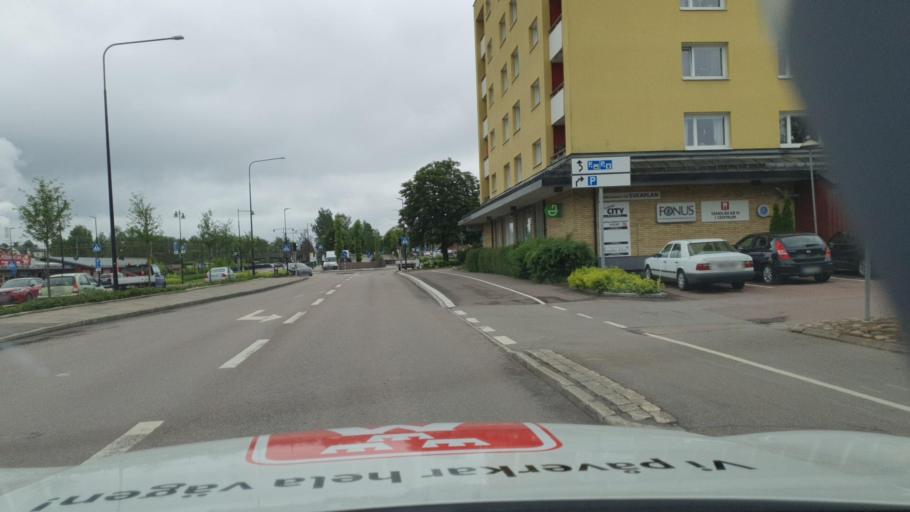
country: SE
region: Vaermland
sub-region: Grums Kommun
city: Grums
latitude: 59.3536
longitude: 13.1130
